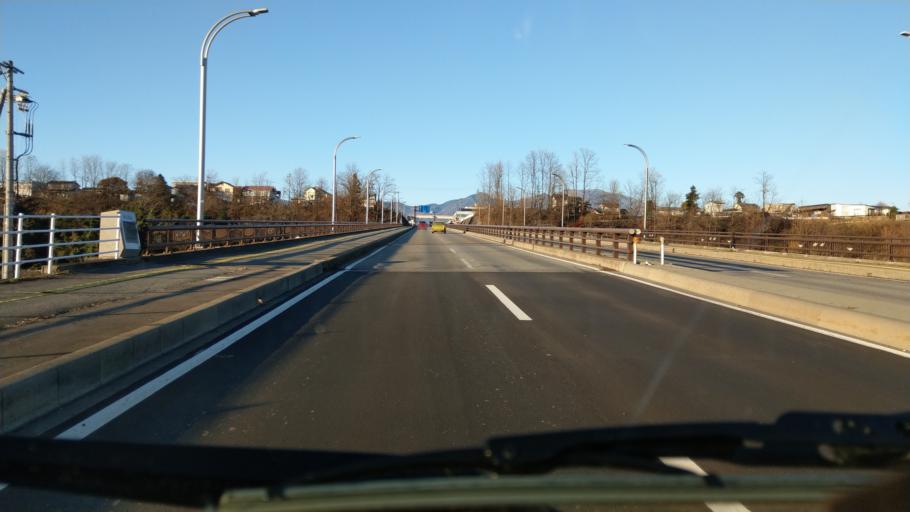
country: JP
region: Nagano
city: Saku
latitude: 36.2458
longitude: 138.4675
